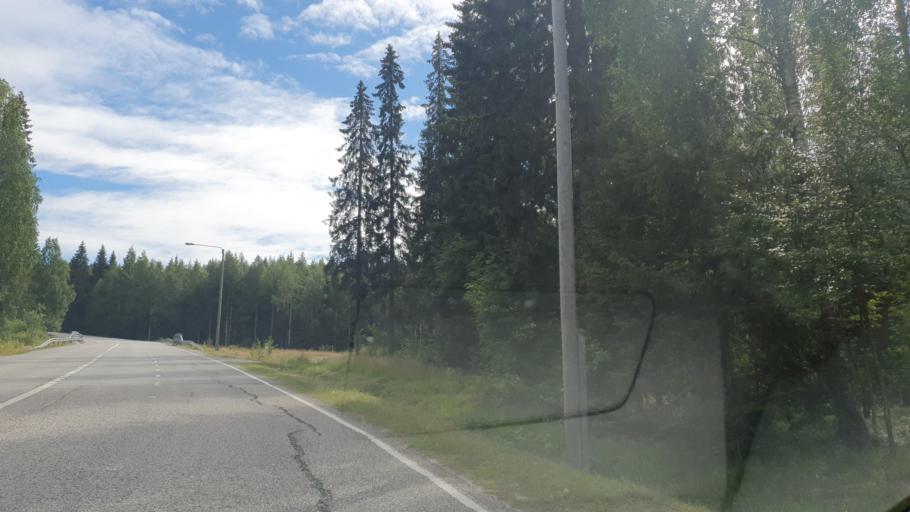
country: FI
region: Kainuu
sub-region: Kajaani
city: Vuokatti
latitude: 64.1308
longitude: 28.2401
